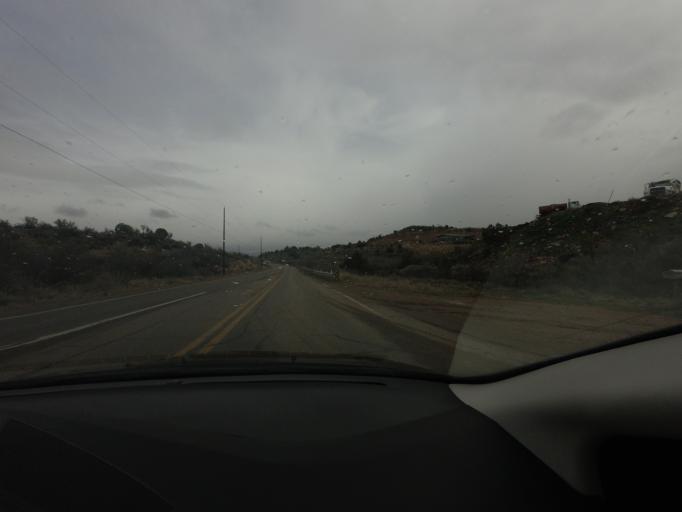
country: US
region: Arizona
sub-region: Yavapai County
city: Lake Montezuma
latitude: 34.6470
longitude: -111.8206
